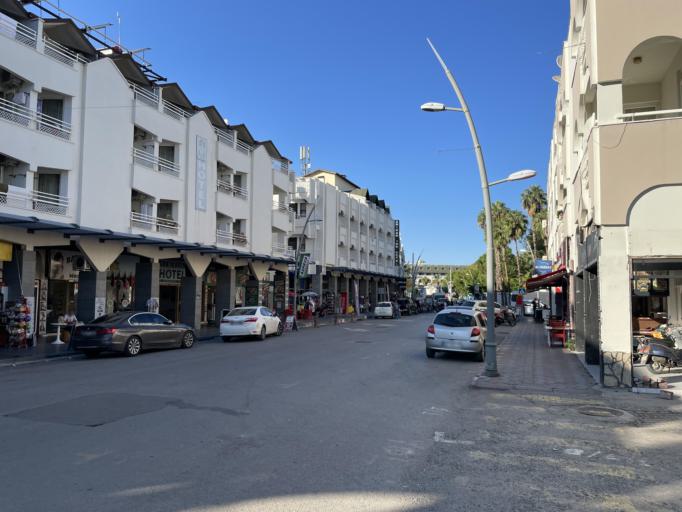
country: TR
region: Antalya
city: Kemer
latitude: 36.5985
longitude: 30.5674
